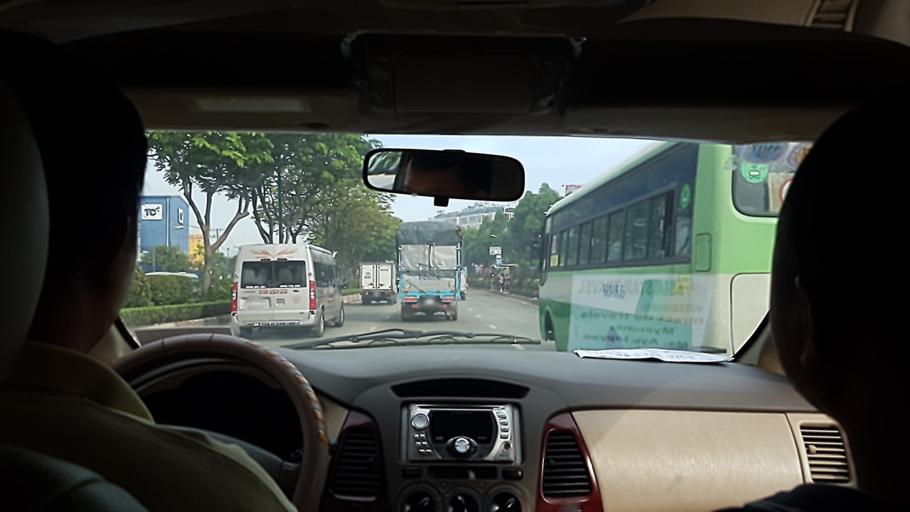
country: VN
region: Ho Chi Minh City
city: Ho Chi Minh City
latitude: 10.8213
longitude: 106.6305
